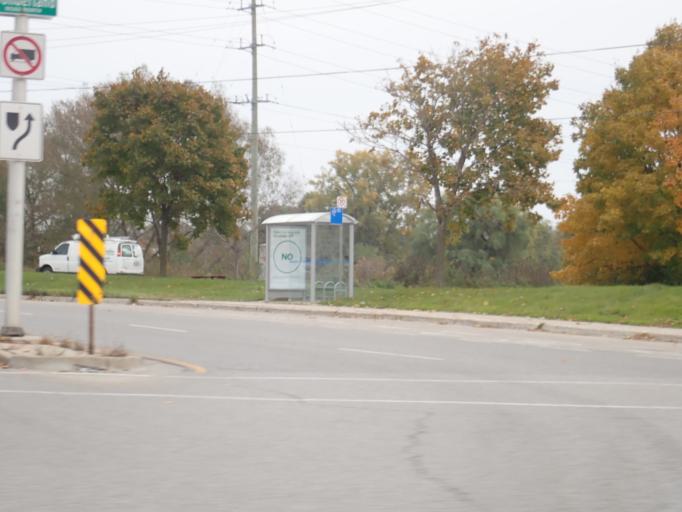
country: CA
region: Ontario
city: London
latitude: 42.9760
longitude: -81.2903
